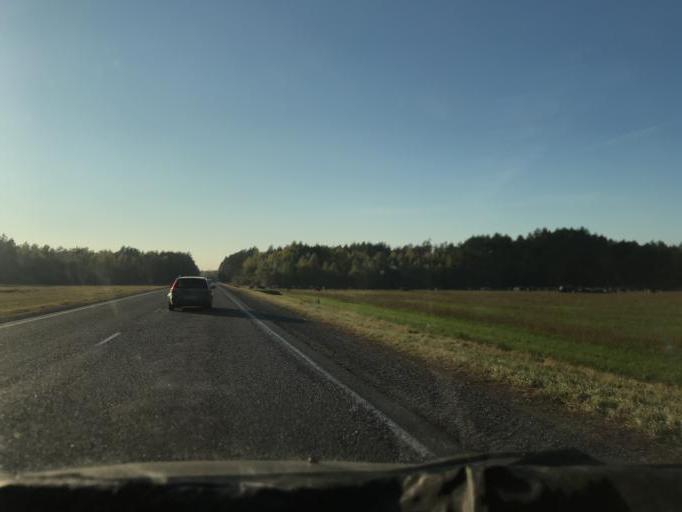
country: BY
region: Gomel
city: Zhytkavichy
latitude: 52.2727
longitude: 28.0216
